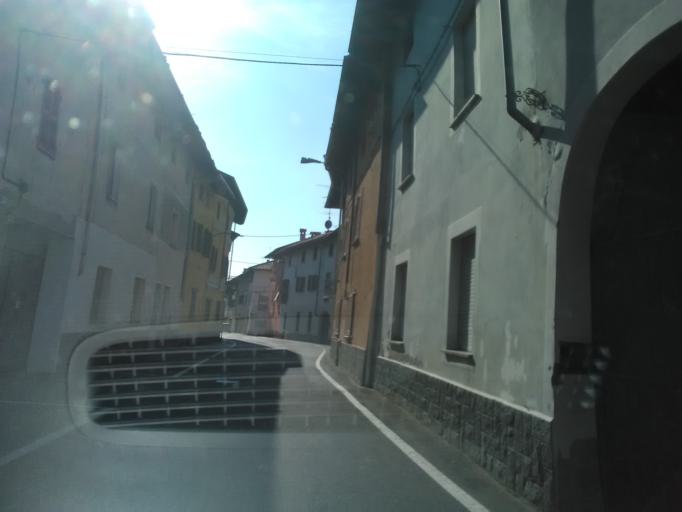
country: IT
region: Piedmont
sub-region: Provincia di Vercelli
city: Lenta
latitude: 45.5566
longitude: 8.3843
